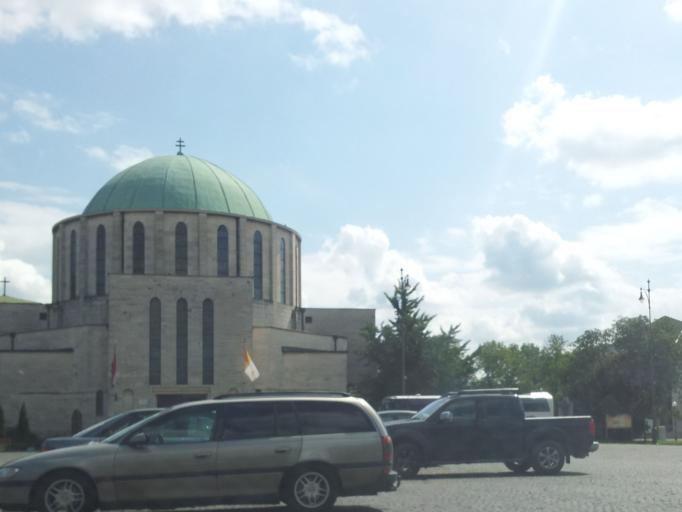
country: HU
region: Baranya
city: Mohacs
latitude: 45.9907
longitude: 18.6891
